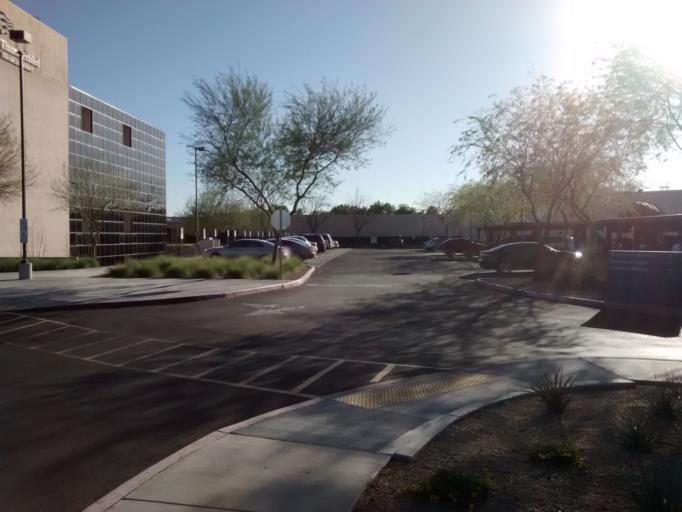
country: US
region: Arizona
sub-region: Maricopa County
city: Peoria
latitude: 33.6101
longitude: -112.1800
